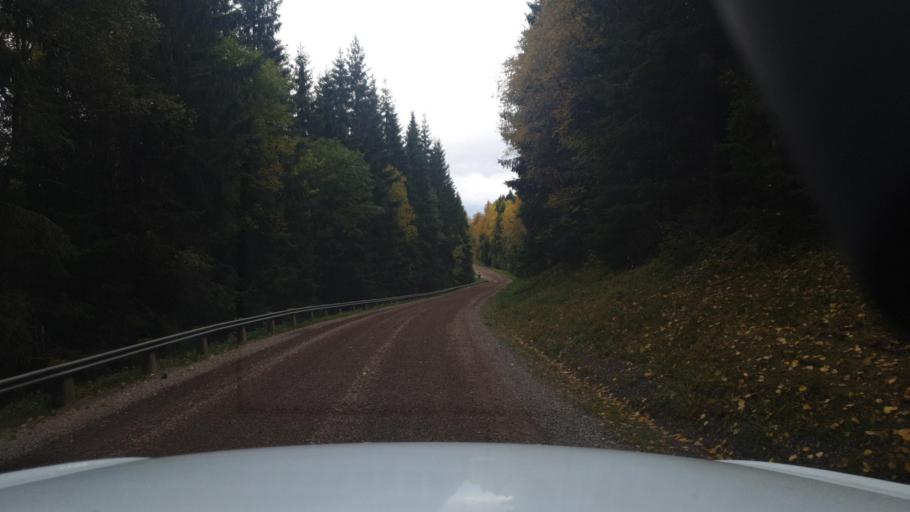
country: SE
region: Vaermland
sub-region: Eda Kommun
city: Charlottenberg
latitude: 60.0620
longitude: 12.5479
